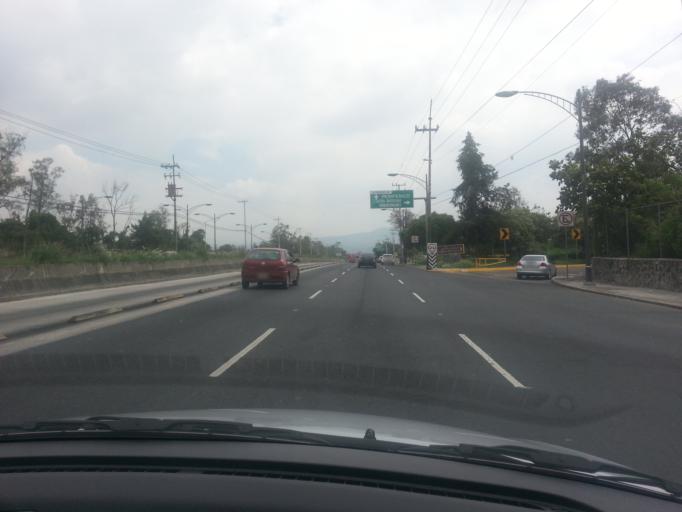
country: MX
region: Mexico City
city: Magdalena Contreras
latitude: 19.3194
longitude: -99.1881
